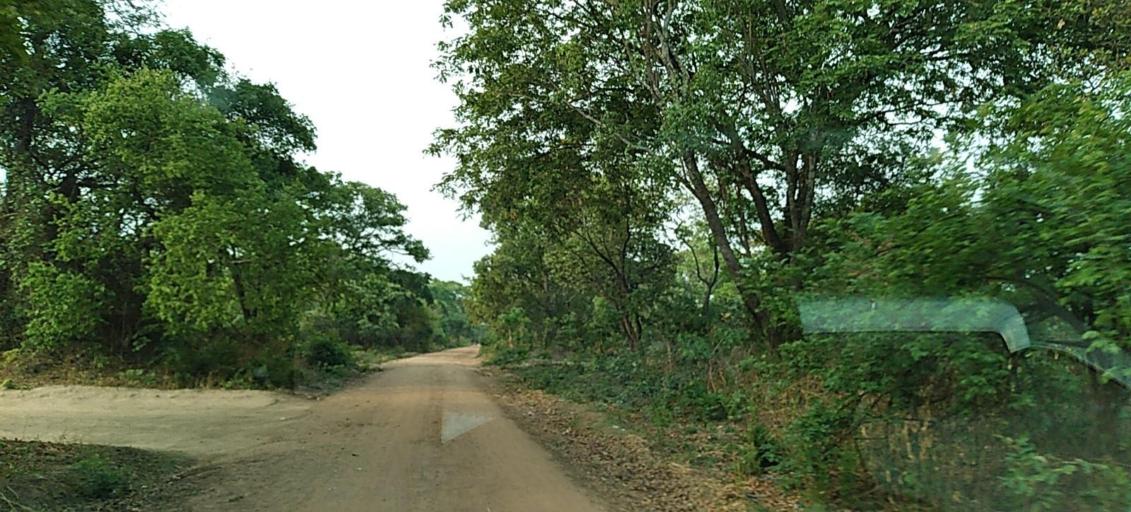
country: ZM
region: Copperbelt
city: Chingola
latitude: -12.8868
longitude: 27.6902
